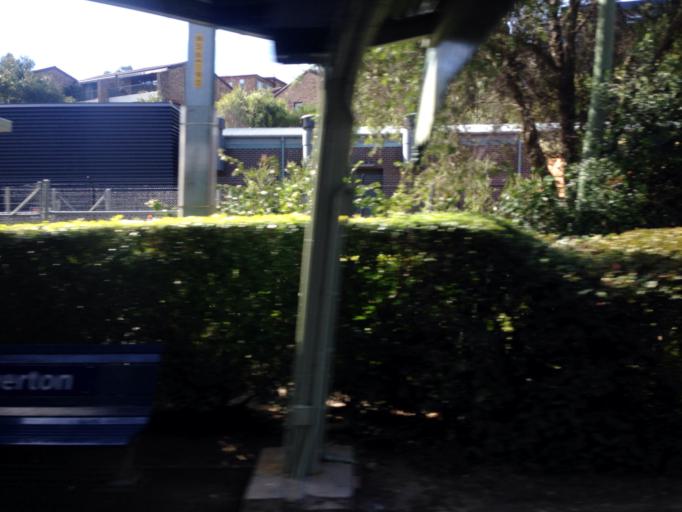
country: AU
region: New South Wales
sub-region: North Sydney
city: North Sydney
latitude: -33.8382
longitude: 151.1977
